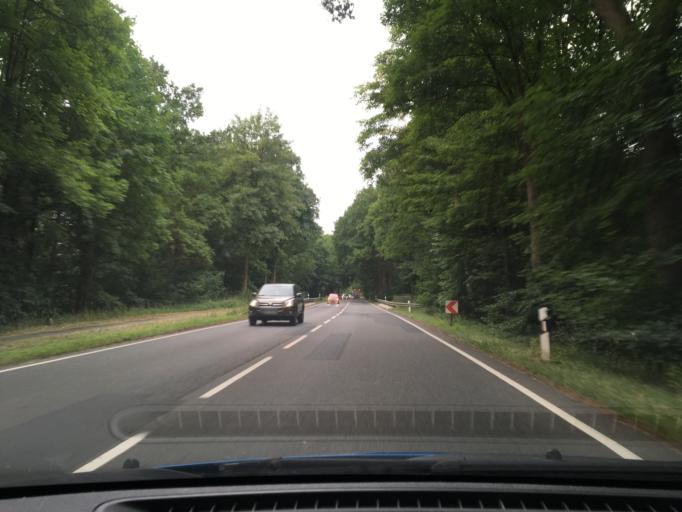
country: DE
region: Lower Saxony
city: Kakenstorf
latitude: 53.3156
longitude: 9.7723
